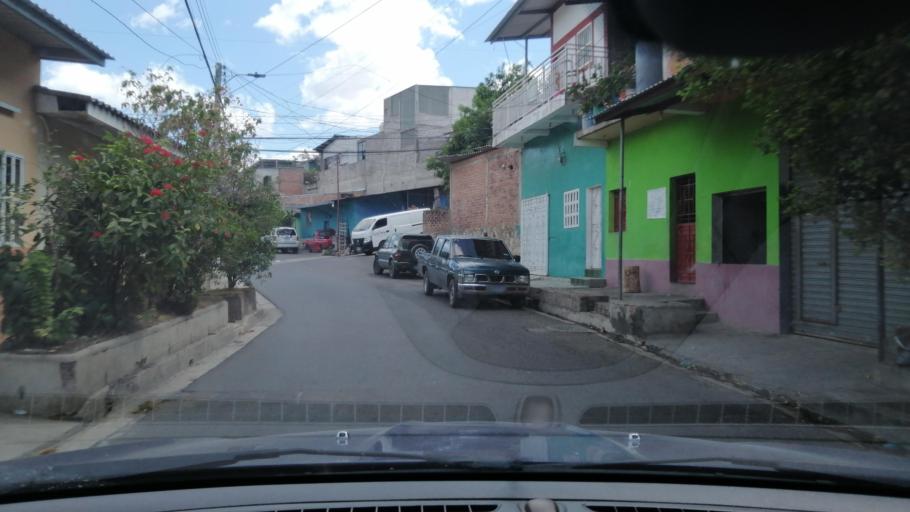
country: SV
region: Santa Ana
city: Metapan
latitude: 14.3305
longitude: -89.4399
